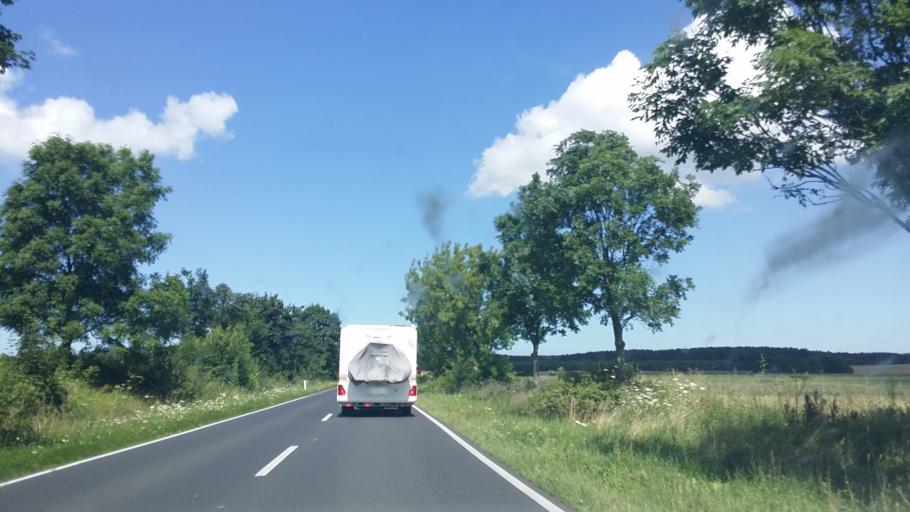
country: PL
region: West Pomeranian Voivodeship
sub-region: Powiat kolobrzeski
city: Goscino
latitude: 54.0893
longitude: 15.6244
